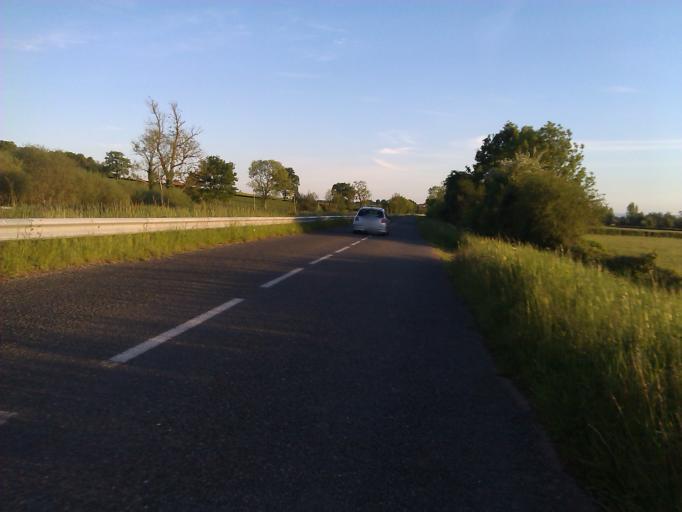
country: FR
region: Bourgogne
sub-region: Departement de Saone-et-Loire
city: Paray-le-Monial
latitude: 46.4853
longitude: 4.1778
